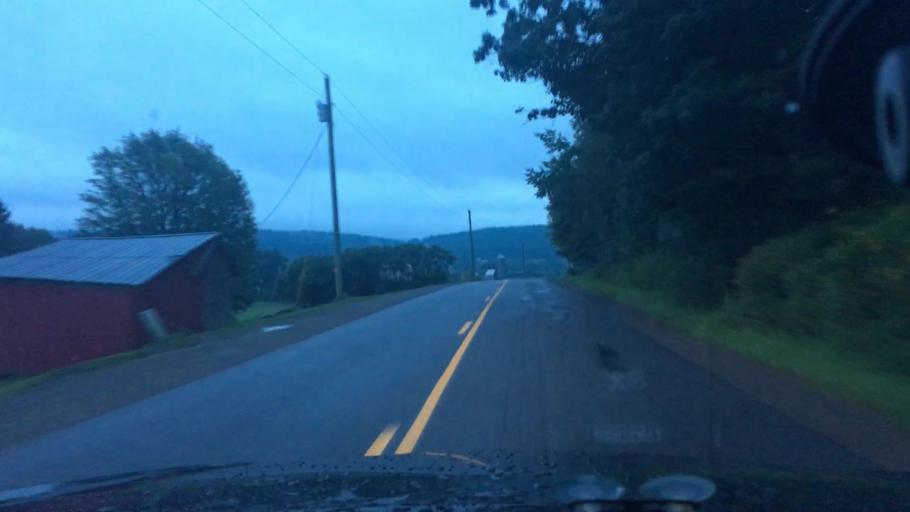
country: US
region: New York
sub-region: Cattaraugus County
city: Little Valley
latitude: 42.2410
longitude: -78.8892
